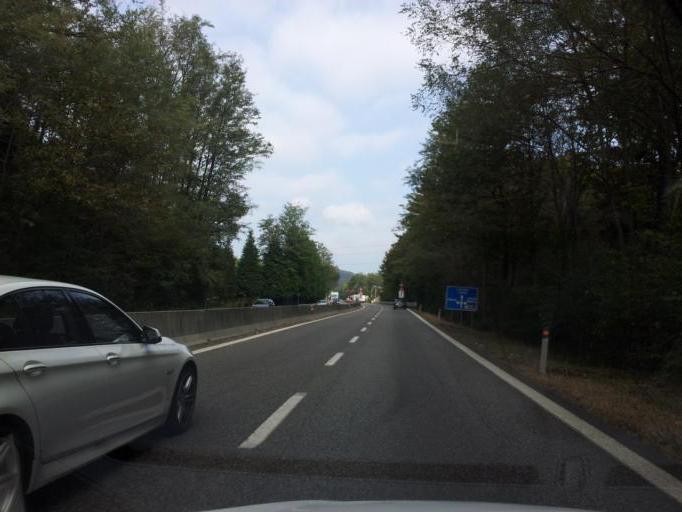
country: IT
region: Lombardy
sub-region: Provincia di Varese
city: Corgeno
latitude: 45.7340
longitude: 8.6800
